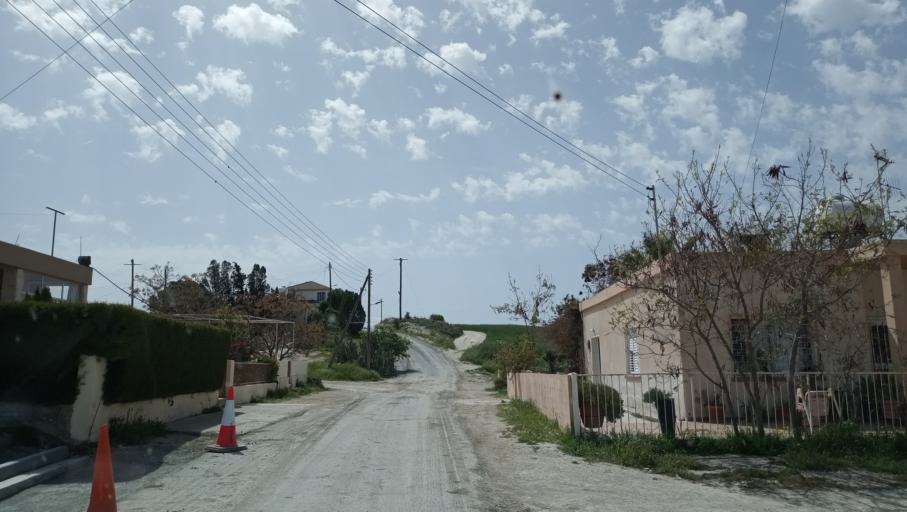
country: CY
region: Lefkosia
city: Dali
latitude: 35.0134
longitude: 33.4212
